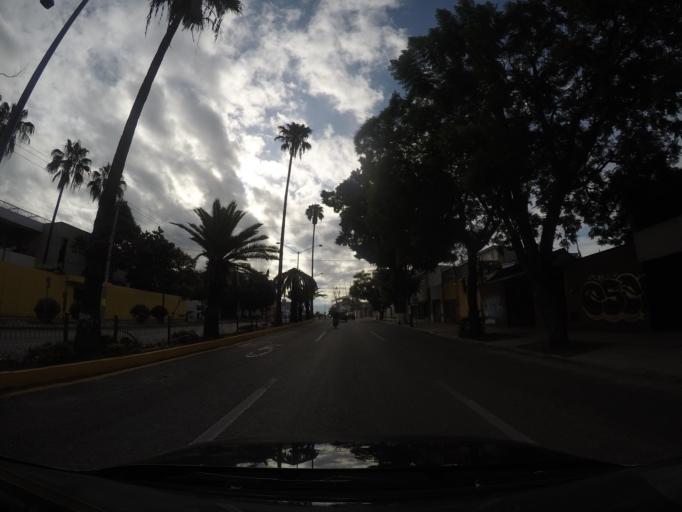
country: MX
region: Oaxaca
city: Oaxaca de Juarez
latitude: 17.0706
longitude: -96.7155
